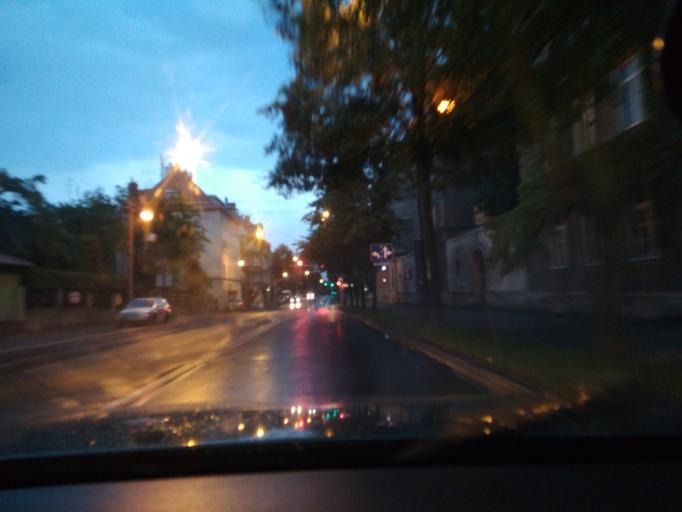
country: PL
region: Silesian Voivodeship
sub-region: Gliwice
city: Gliwice
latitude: 50.2959
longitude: 18.6511
